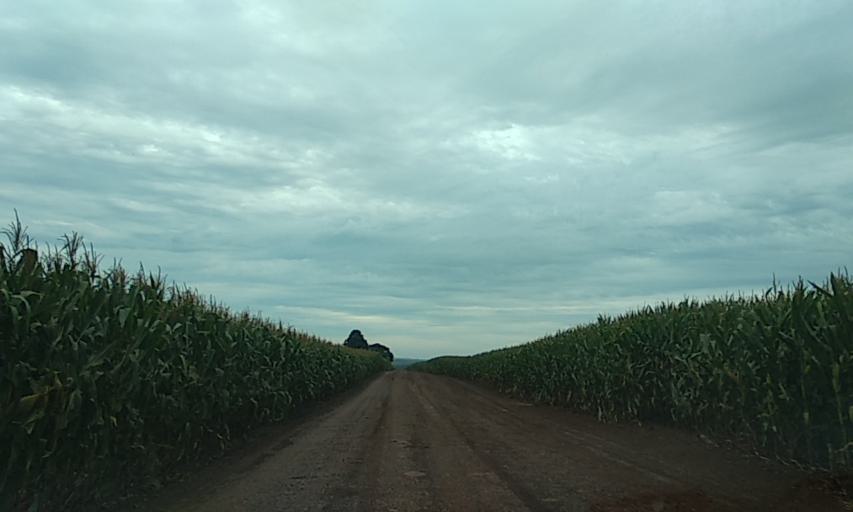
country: BR
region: Parana
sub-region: Marechal Candido Rondon
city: Marechal Candido Rondon
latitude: -24.5389
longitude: -54.0934
